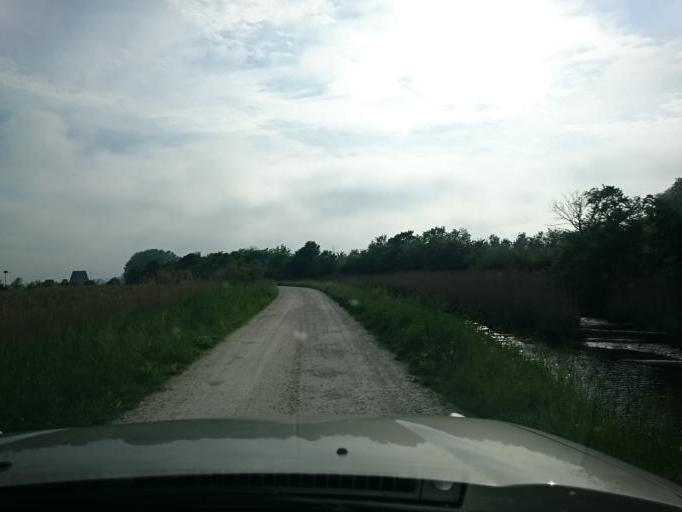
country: IT
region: Veneto
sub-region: Provincia di Padova
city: Codevigo
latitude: 45.2647
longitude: 12.1488
